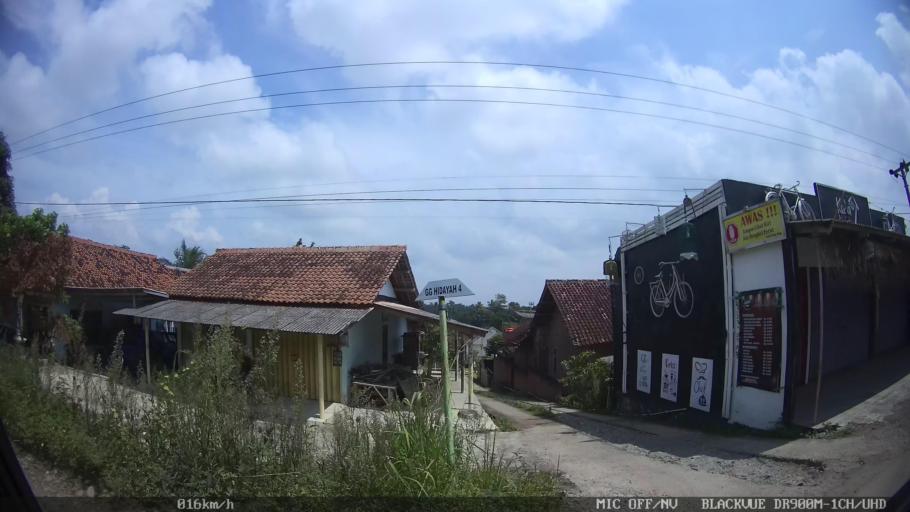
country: ID
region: Lampung
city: Kedaton
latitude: -5.3370
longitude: 105.2974
